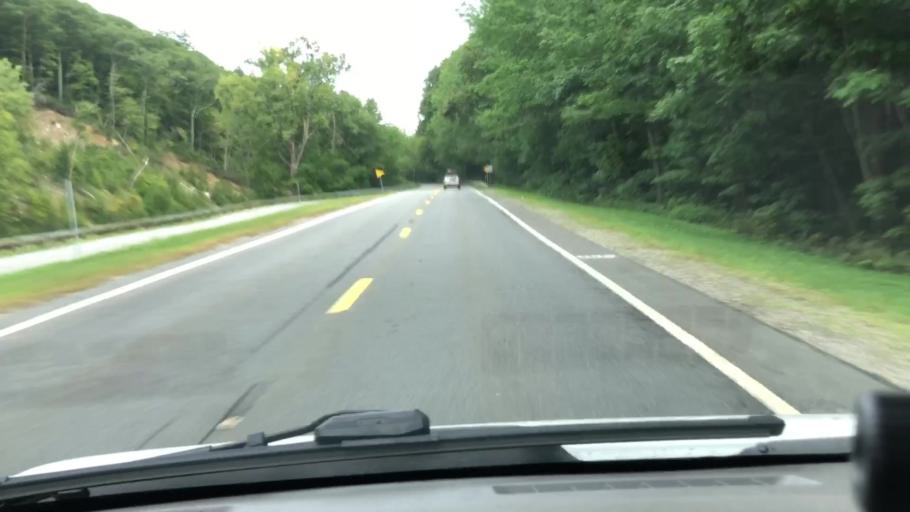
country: US
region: Massachusetts
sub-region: Franklin County
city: Charlemont
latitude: 42.6411
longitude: -72.9593
